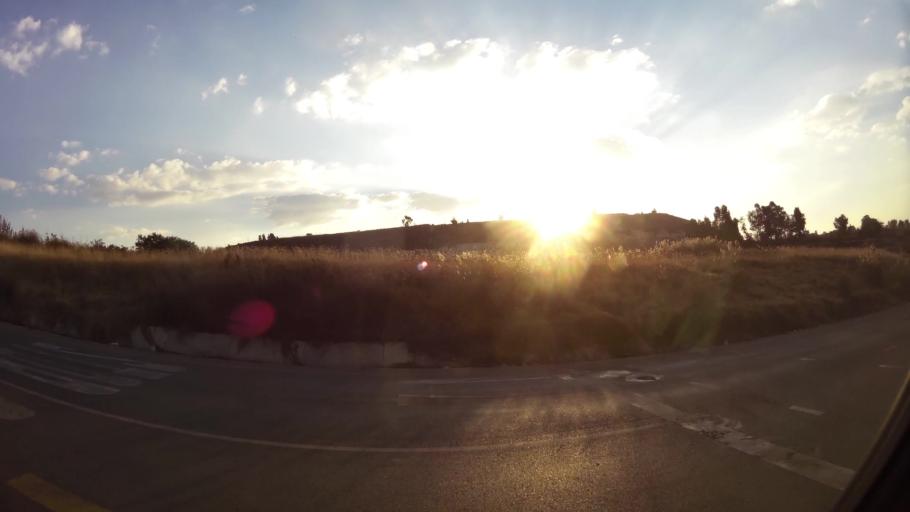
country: ZA
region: Gauteng
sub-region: City of Johannesburg Metropolitan Municipality
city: Roodepoort
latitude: -26.2075
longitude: 27.9041
